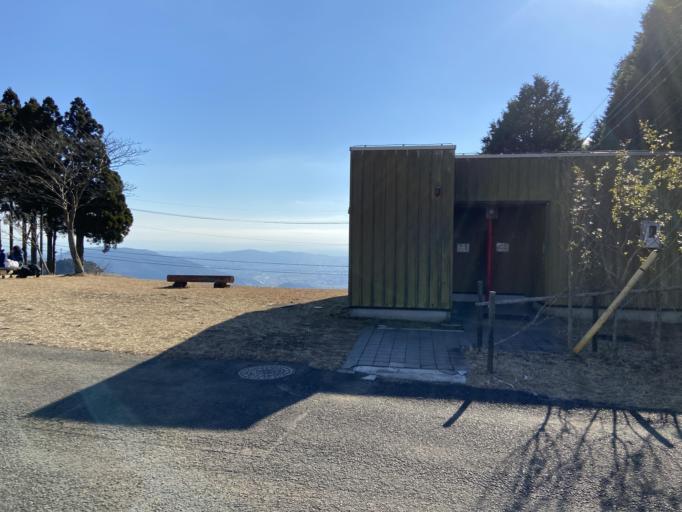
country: JP
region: Shizuoka
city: Gotemba
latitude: 35.3867
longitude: 139.0489
